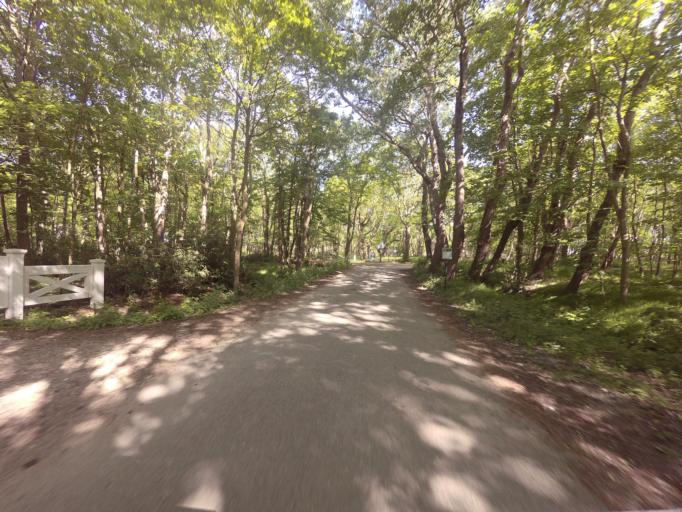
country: NL
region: Zeeland
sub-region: Gemeente Middelburg
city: Middelburg
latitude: 51.5765
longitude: 3.5344
